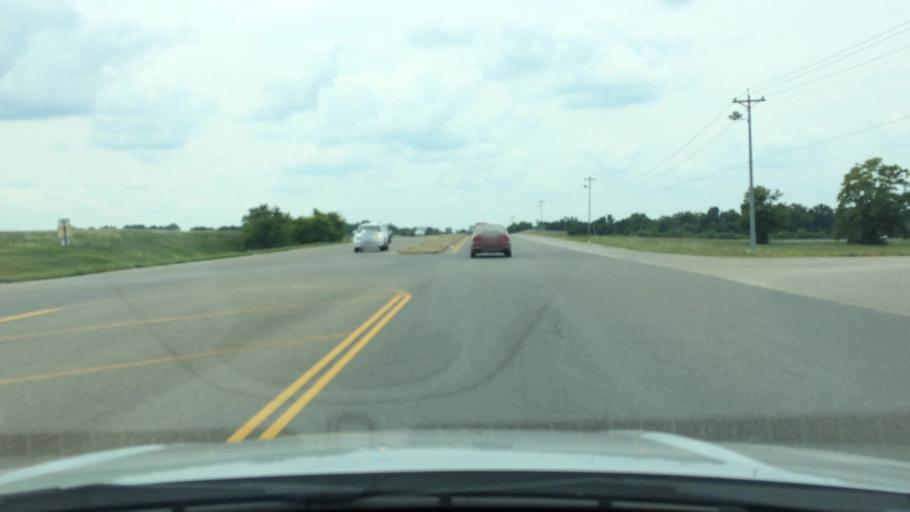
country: US
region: Tennessee
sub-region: Maury County
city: Spring Hill
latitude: 35.7364
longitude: -86.8938
